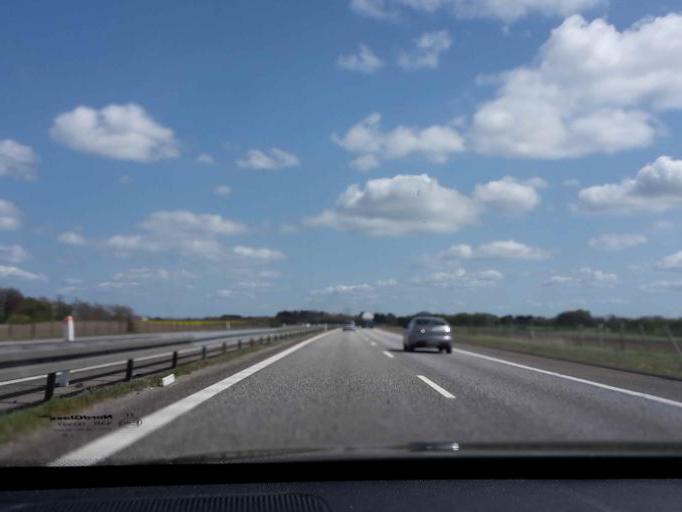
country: DK
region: South Denmark
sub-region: Vejen Kommune
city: Vejen
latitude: 55.4977
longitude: 9.2144
